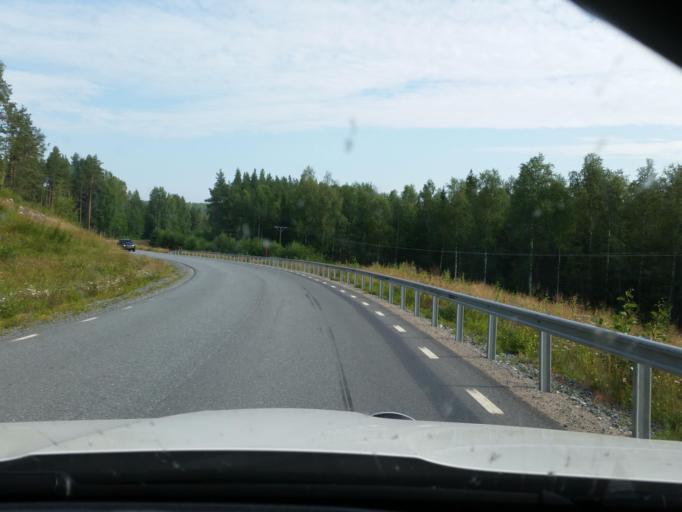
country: SE
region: Norrbotten
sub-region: Alvsbyns Kommun
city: AElvsbyn
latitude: 65.6604
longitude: 20.8775
